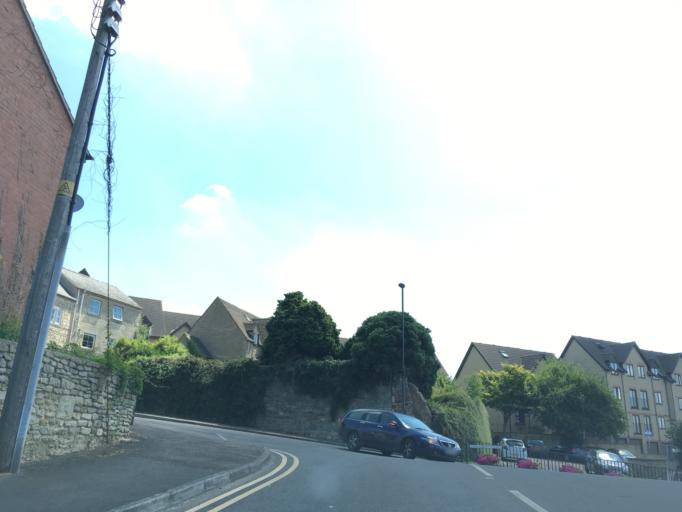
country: GB
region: England
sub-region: Gloucestershire
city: Stroud
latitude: 51.7455
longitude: -2.2133
